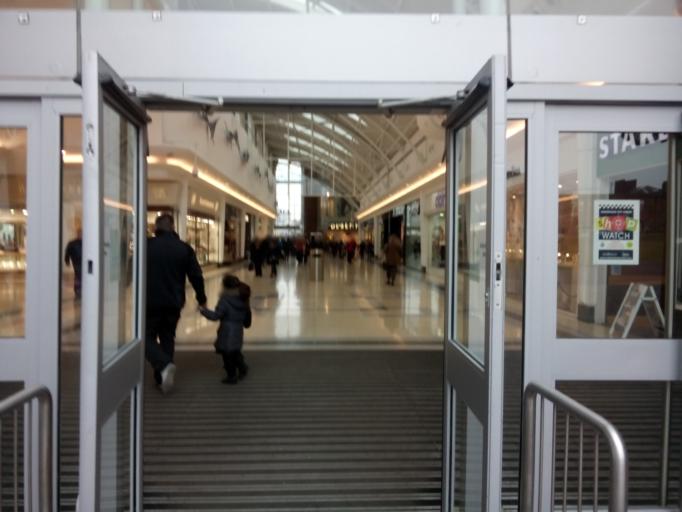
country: GB
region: England
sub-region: Sunderland
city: Sunderland
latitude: 54.9058
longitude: -1.3863
